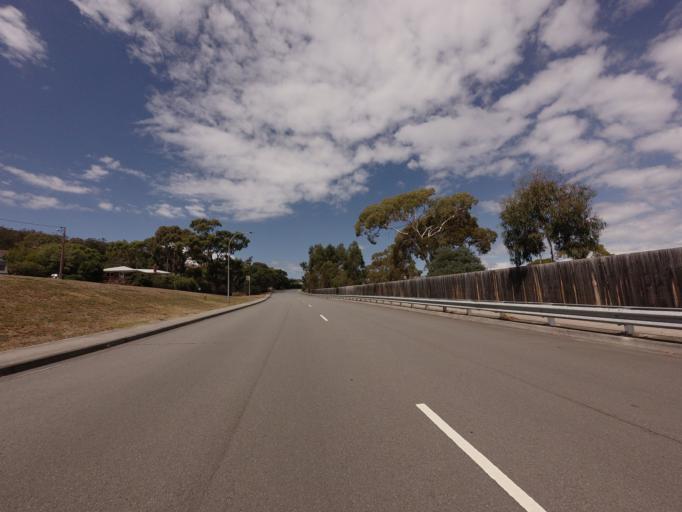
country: AU
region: Tasmania
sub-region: Clarence
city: Howrah
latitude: -42.8948
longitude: 147.4147
